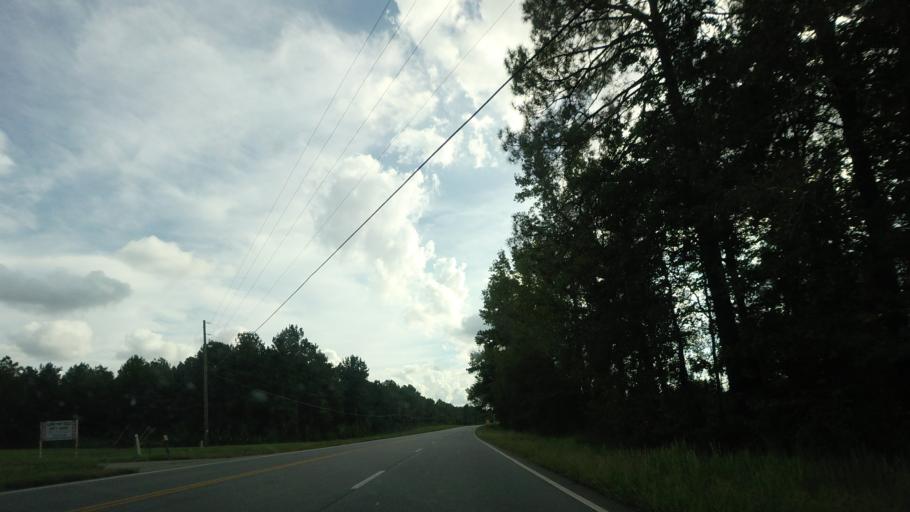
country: US
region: Georgia
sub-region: Pulaski County
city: Hawkinsville
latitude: 32.3093
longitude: -83.4219
